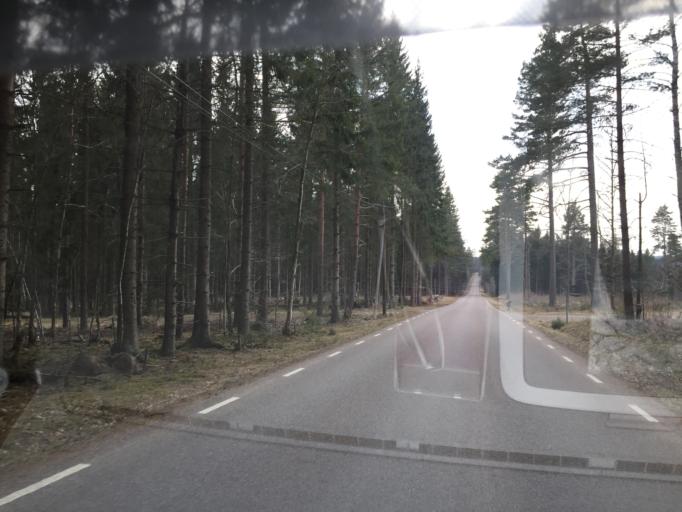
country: SE
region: Soedermanland
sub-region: Vingakers Kommun
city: Vingaker
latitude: 59.0165
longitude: 15.6775
